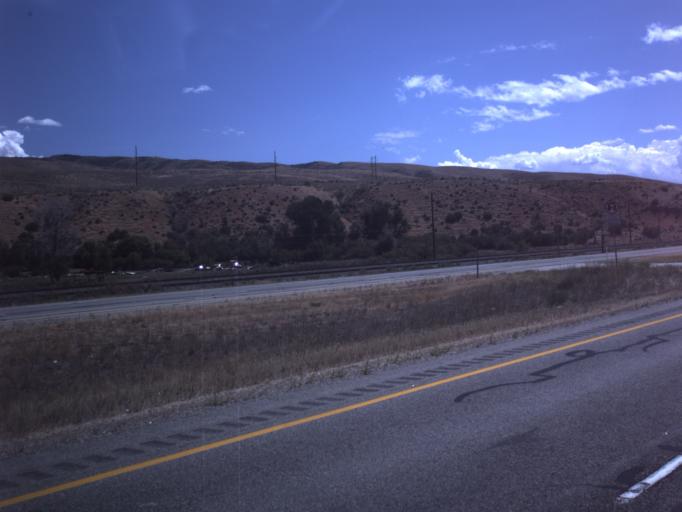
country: US
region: Utah
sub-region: Summit County
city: Coalville
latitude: 41.0229
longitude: -111.4955
